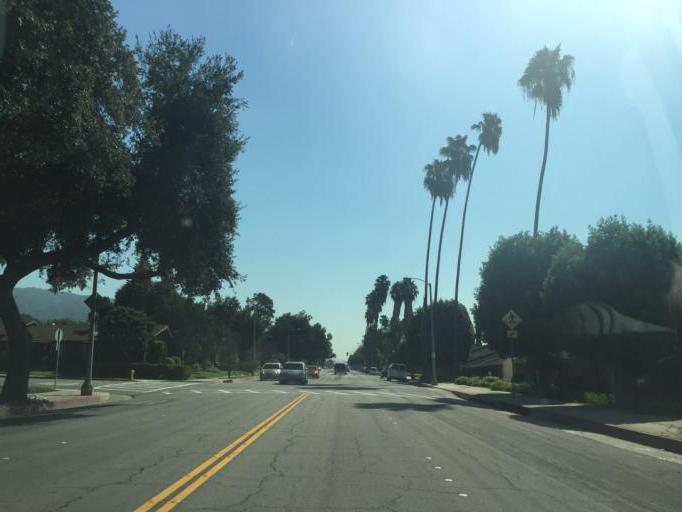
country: US
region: California
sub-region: Los Angeles County
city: Monrovia
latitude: 34.1512
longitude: -118.0159
